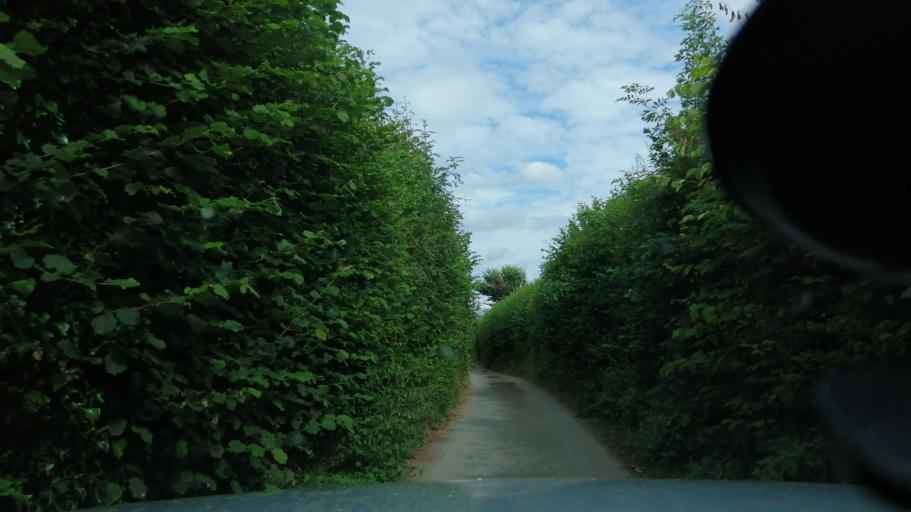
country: GB
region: England
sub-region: Herefordshire
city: Thruxton
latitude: 52.0112
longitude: -2.7981
